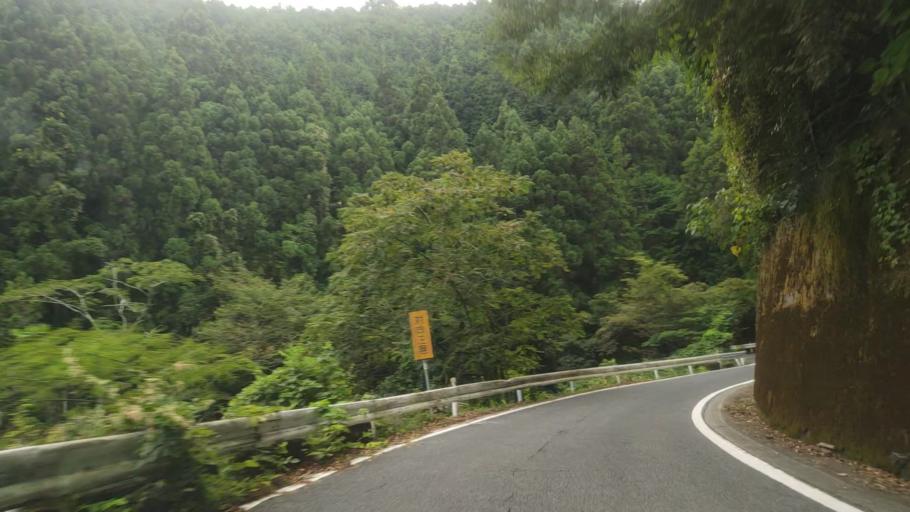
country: JP
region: Wakayama
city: Koya
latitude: 34.2382
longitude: 135.5466
